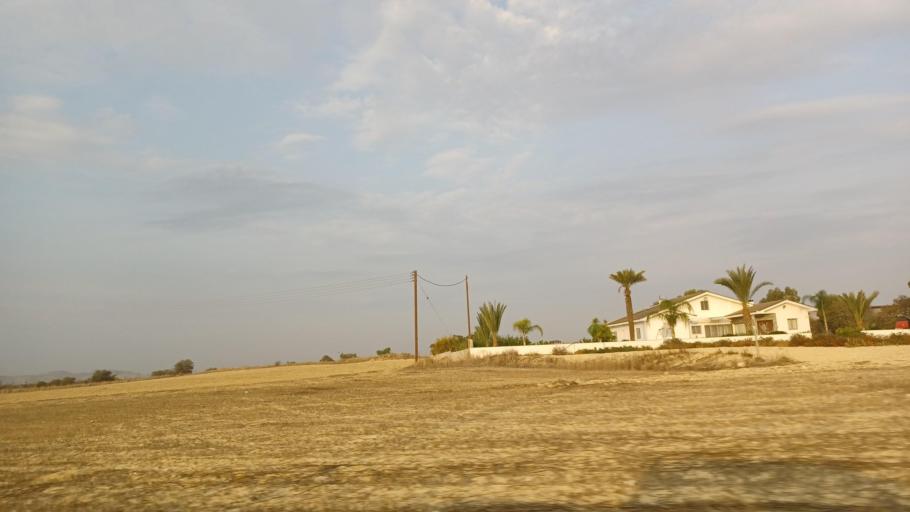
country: CY
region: Larnaka
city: Athienou
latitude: 35.0606
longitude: 33.5275
